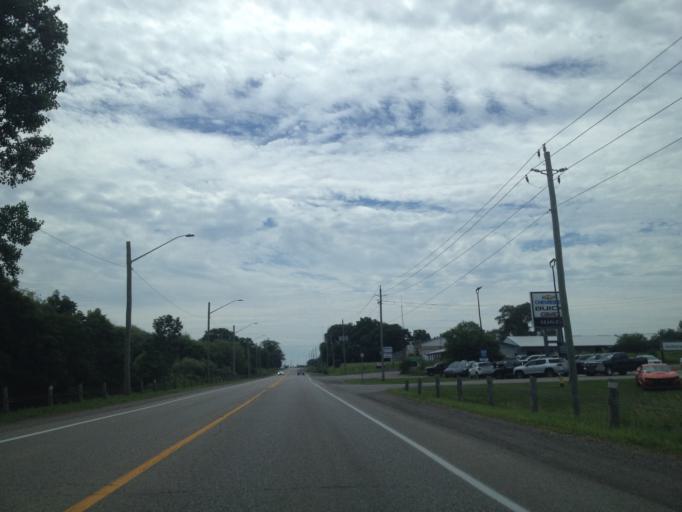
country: CA
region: Ontario
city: Ingersoll
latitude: 43.0338
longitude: -80.8623
